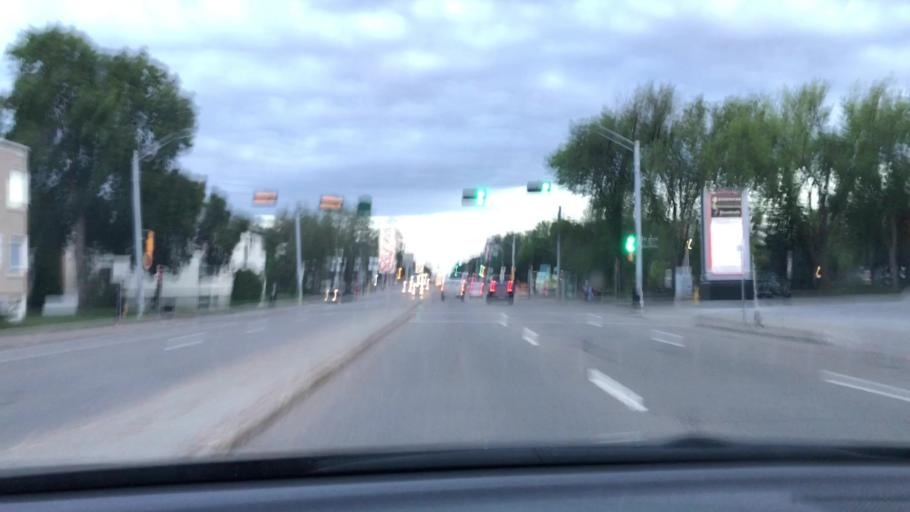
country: CA
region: Alberta
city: Edmonton
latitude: 53.5206
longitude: -113.5121
